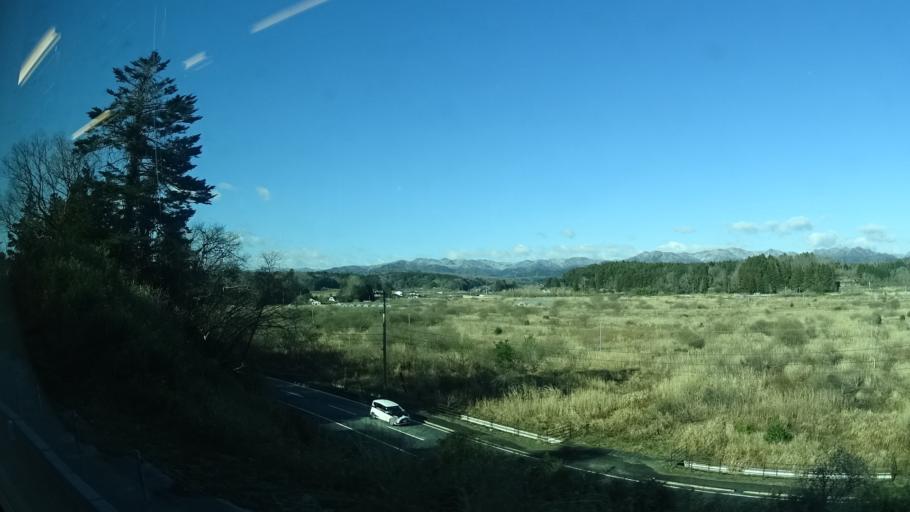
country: JP
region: Fukushima
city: Namie
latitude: 37.4354
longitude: 141.0007
